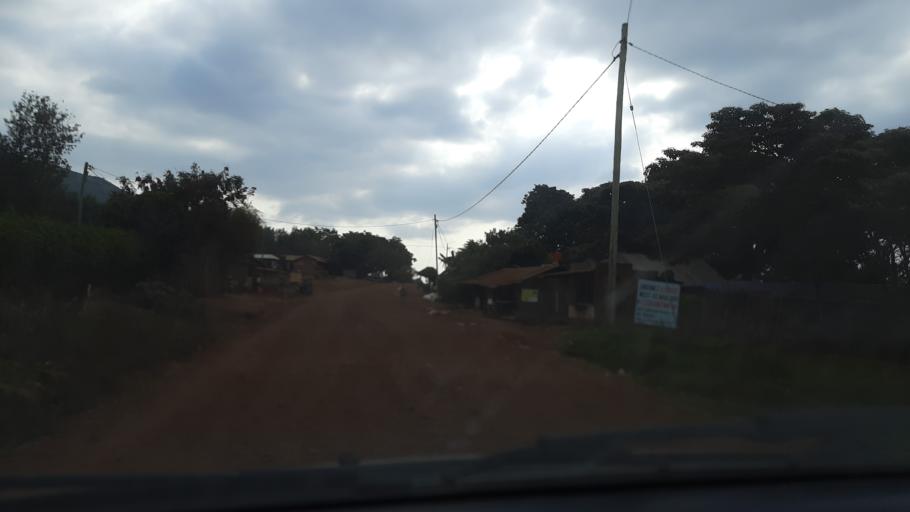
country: TZ
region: Arusha
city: Kingori
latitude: -2.8497
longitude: 37.2071
